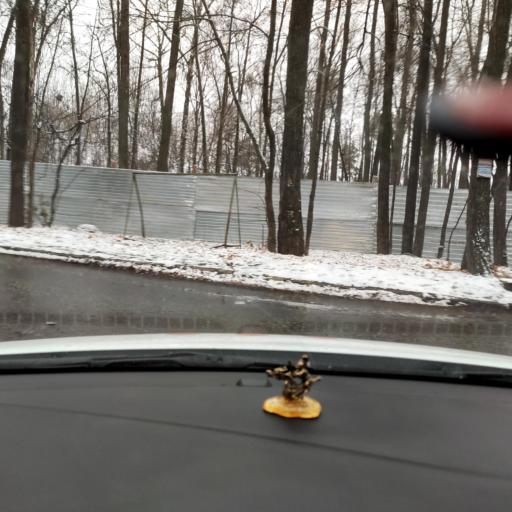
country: RU
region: Tatarstan
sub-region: Zelenodol'skiy Rayon
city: Zelenodolsk
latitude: 55.8444
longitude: 48.5086
